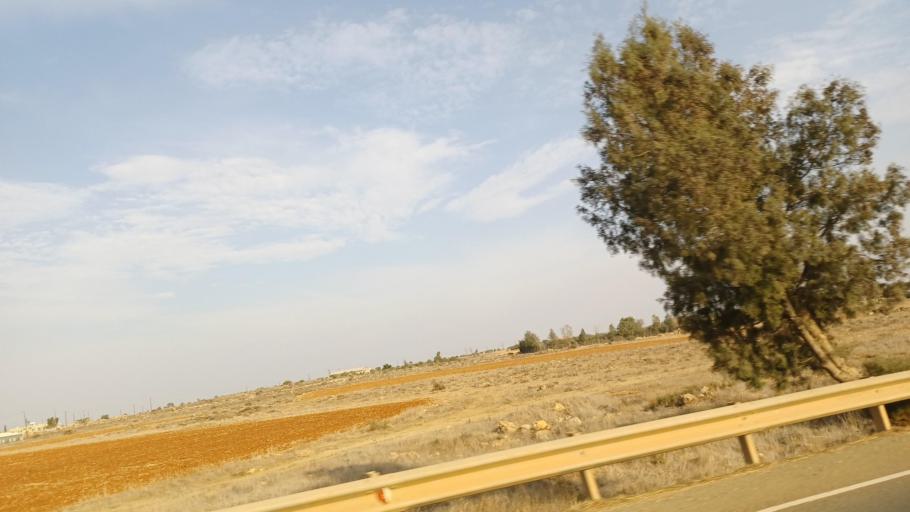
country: CY
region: Ammochostos
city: Frenaros
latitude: 35.0593
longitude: 33.8974
